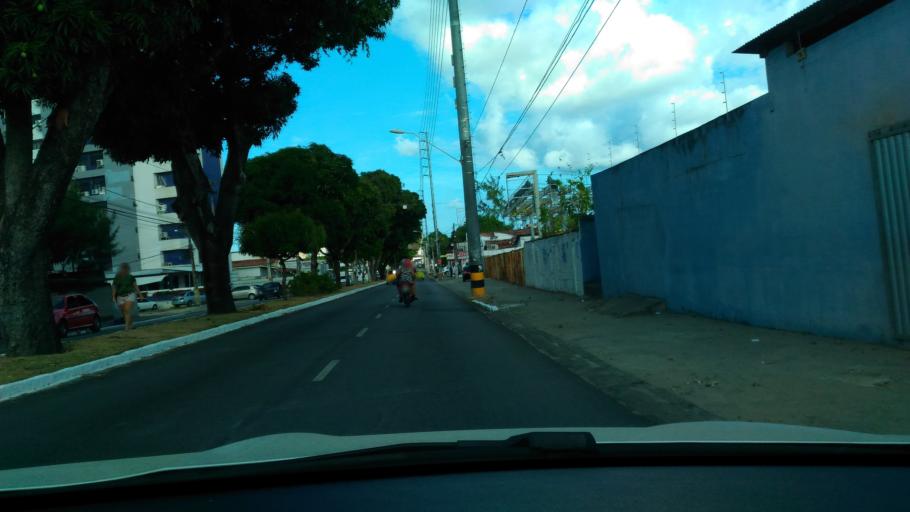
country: BR
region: Paraiba
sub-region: Joao Pessoa
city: Joao Pessoa
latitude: -7.1263
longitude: -34.8778
